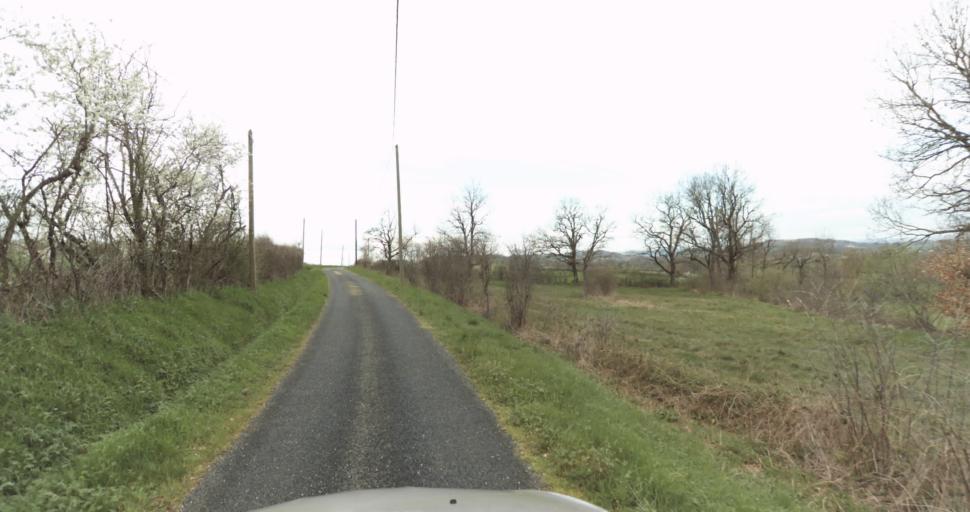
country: FR
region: Midi-Pyrenees
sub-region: Departement du Tarn
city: Frejairolles
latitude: 43.8701
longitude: 2.2092
